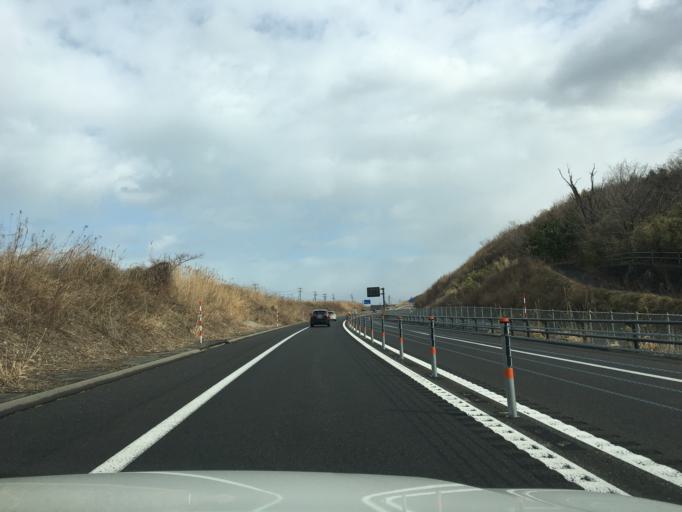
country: JP
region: Yamagata
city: Yuza
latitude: 39.3019
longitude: 139.9775
